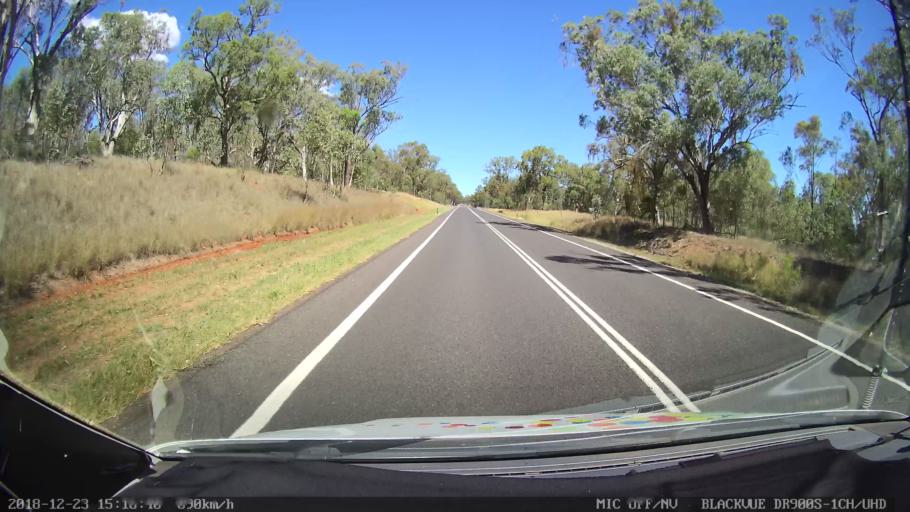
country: AU
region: New South Wales
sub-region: Tamworth Municipality
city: Manilla
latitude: -30.8015
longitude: 150.7499
